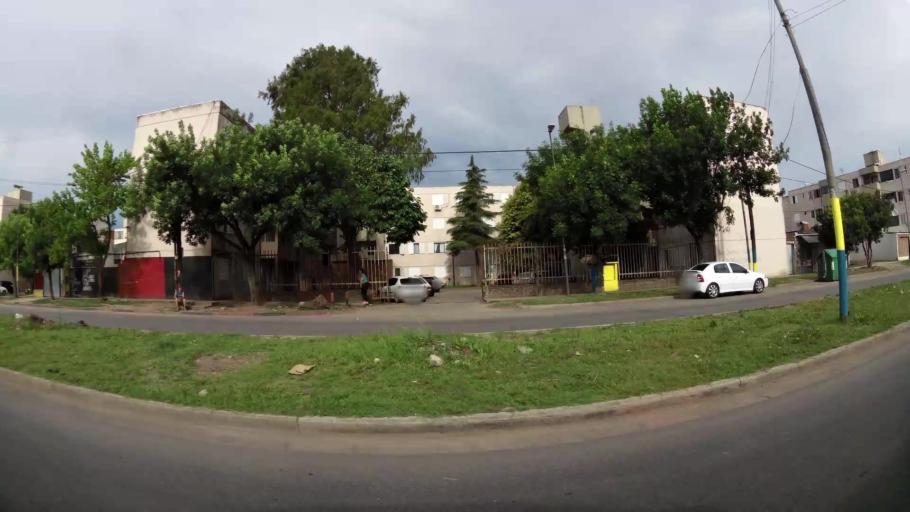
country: AR
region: Santa Fe
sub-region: Departamento de Rosario
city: Rosario
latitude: -32.9840
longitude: -60.6886
